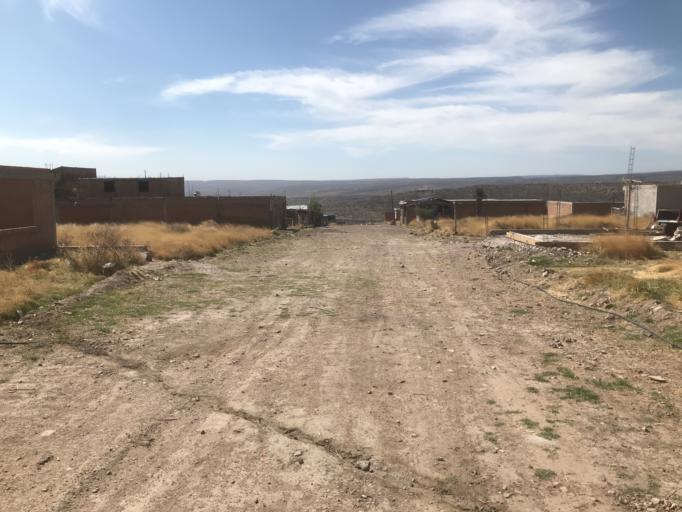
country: MX
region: Durango
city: Victoria de Durango
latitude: 24.0358
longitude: -104.7121
